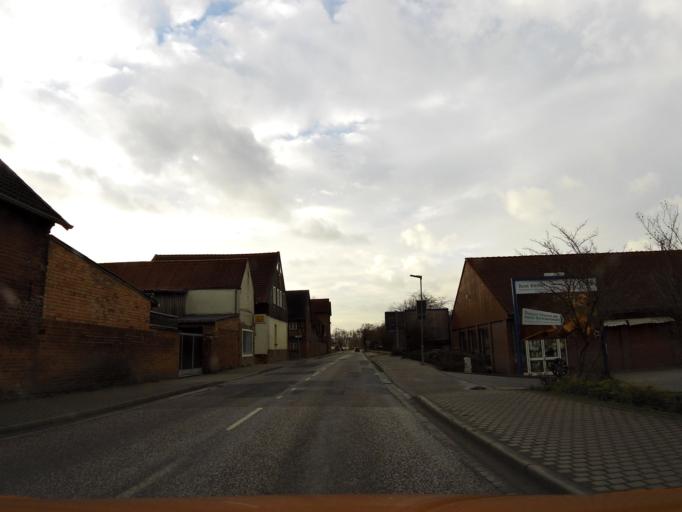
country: DE
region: Saxony-Anhalt
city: Weferlingen
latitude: 52.3111
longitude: 11.0574
